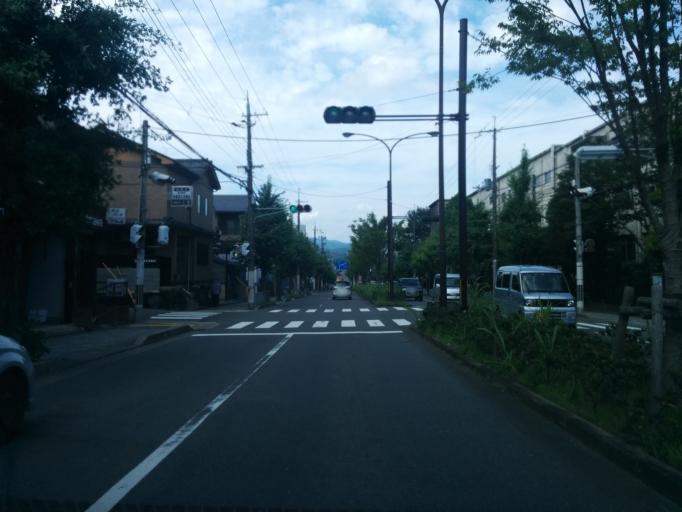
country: JP
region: Kyoto
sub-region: Kyoto-shi
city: Kamigyo-ku
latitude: 35.0469
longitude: 135.7396
